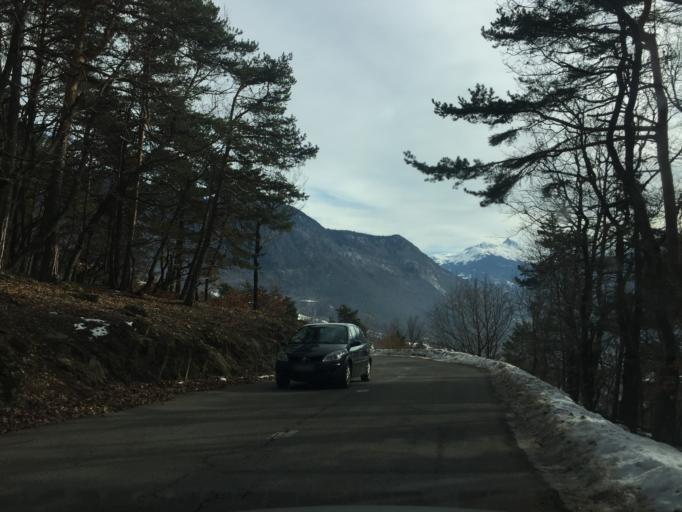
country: FR
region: Rhone-Alpes
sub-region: Departement de la Savoie
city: Aigueblanche
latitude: 45.5308
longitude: 6.4874
